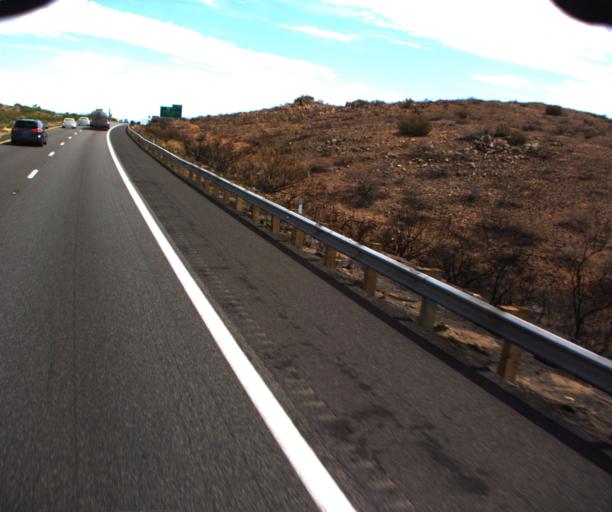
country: US
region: Arizona
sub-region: Yavapai County
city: Cordes Lakes
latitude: 34.3061
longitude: -112.1273
